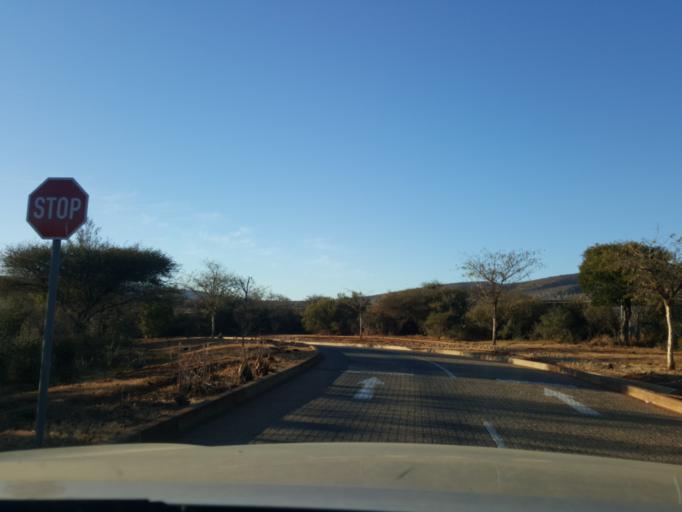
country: BW
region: South East
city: Lobatse
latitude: -25.2822
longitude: 25.7190
